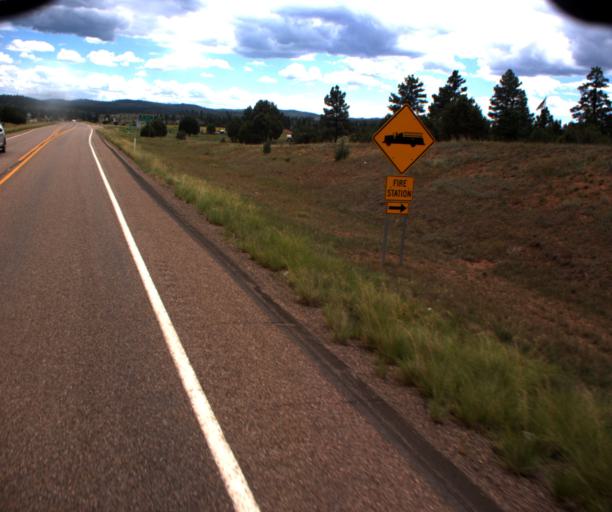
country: US
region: Arizona
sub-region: Navajo County
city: Linden
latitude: 34.3197
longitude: -110.2498
